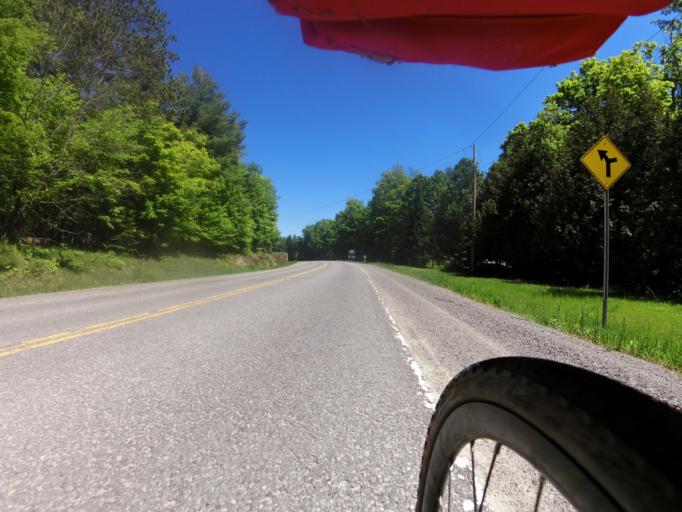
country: CA
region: Ontario
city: Carleton Place
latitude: 45.1856
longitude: -76.3436
